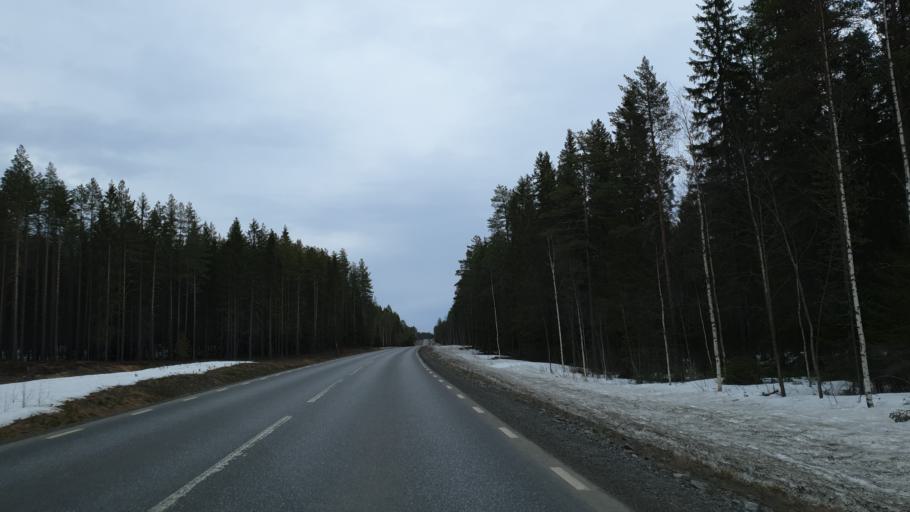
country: SE
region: Vaesterbotten
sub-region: Robertsfors Kommun
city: Robertsfors
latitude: 64.2149
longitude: 20.8924
